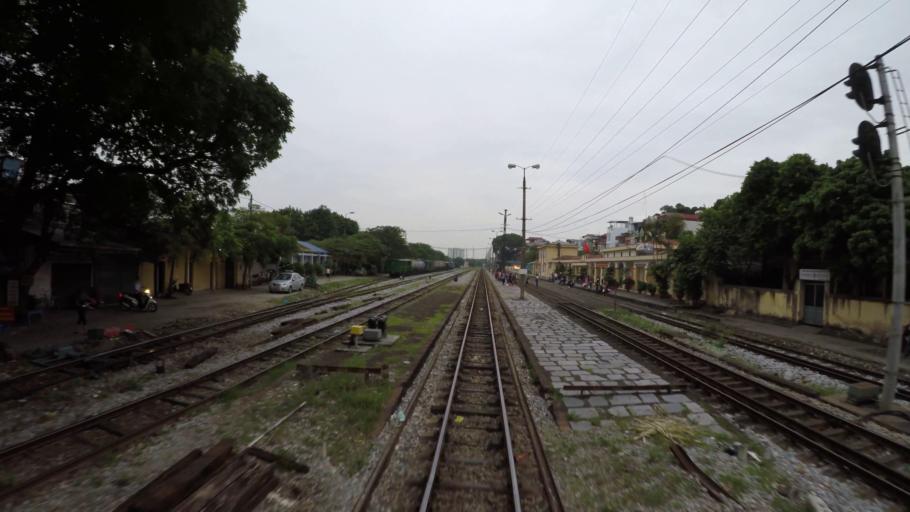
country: VN
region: Ha Noi
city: Trau Quy
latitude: 21.0338
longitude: 105.9054
